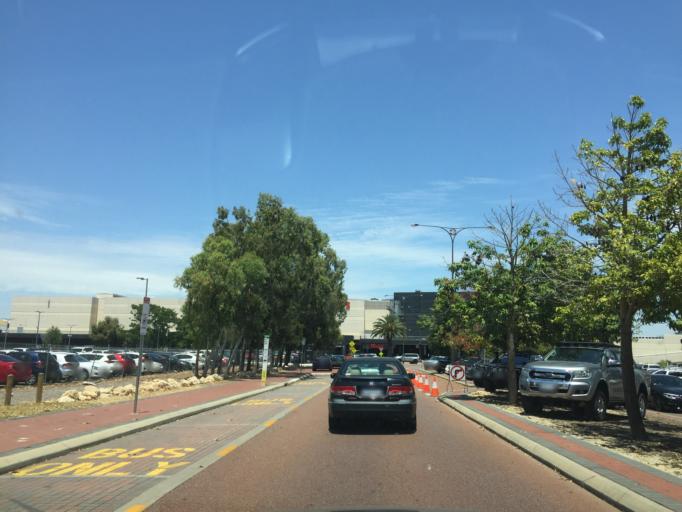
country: AU
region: Western Australia
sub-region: Canning
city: Cannington
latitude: -32.0186
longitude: 115.9402
